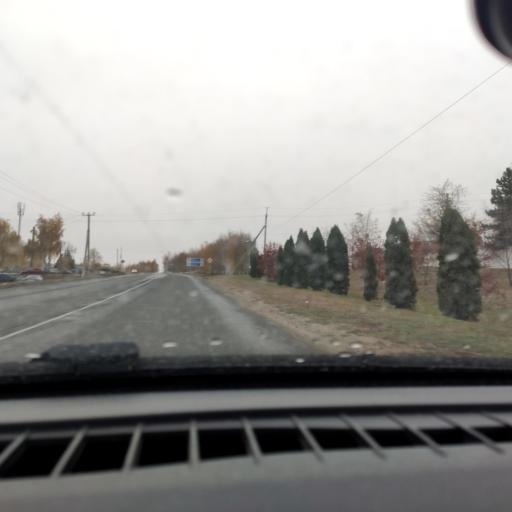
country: RU
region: Belgorod
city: Alekseyevka
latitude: 50.6438
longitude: 38.6879
